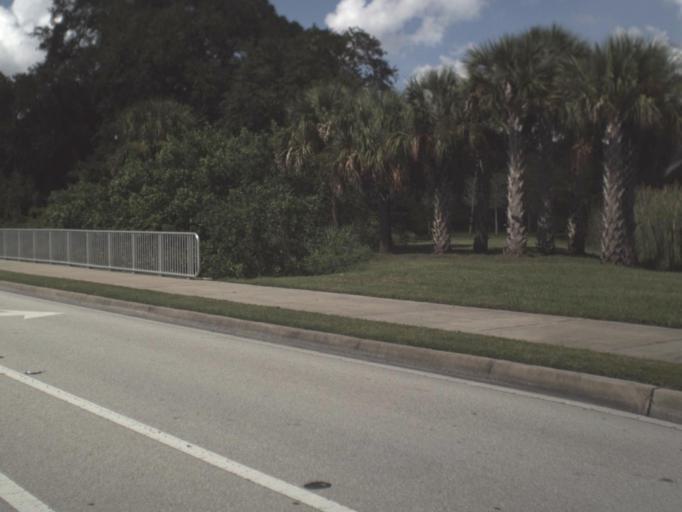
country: US
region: Florida
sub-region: Sarasota County
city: Laurel
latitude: 27.1365
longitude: -82.4568
